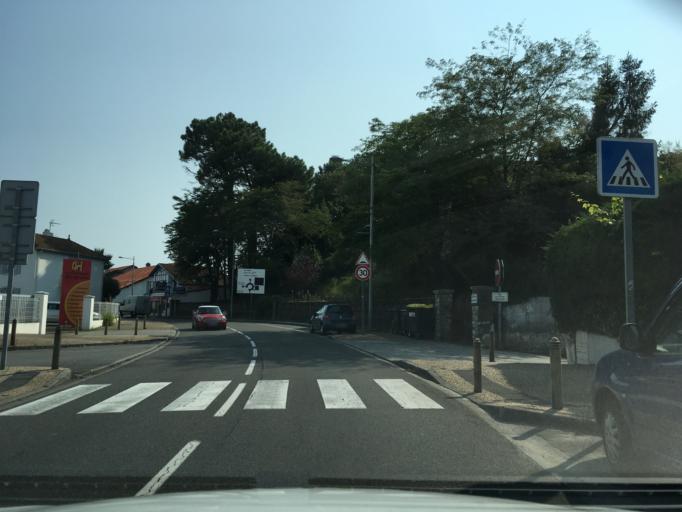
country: FR
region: Aquitaine
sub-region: Departement des Pyrenees-Atlantiques
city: Bayonne
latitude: 43.5116
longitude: -1.5003
